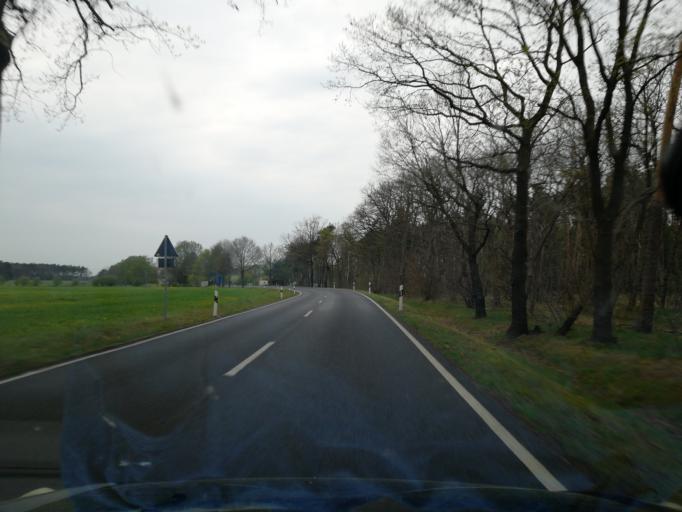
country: DE
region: Brandenburg
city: Calau
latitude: 51.7820
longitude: 13.8847
